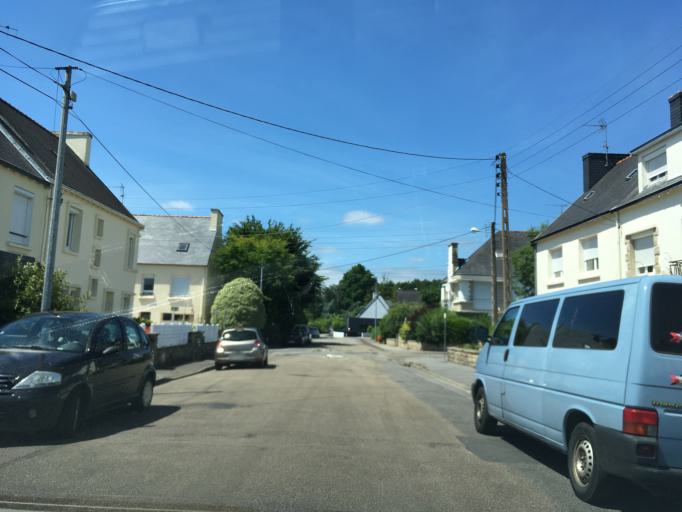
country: FR
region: Brittany
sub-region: Departement du Finistere
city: Quimper
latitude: 48.0046
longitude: -4.1129
